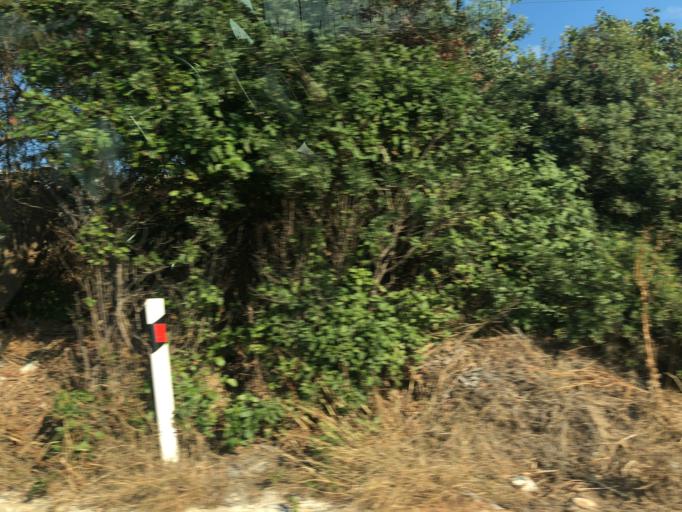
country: GR
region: Crete
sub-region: Nomos Rethymnis
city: Atsipopoulon
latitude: 35.3645
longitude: 24.4227
